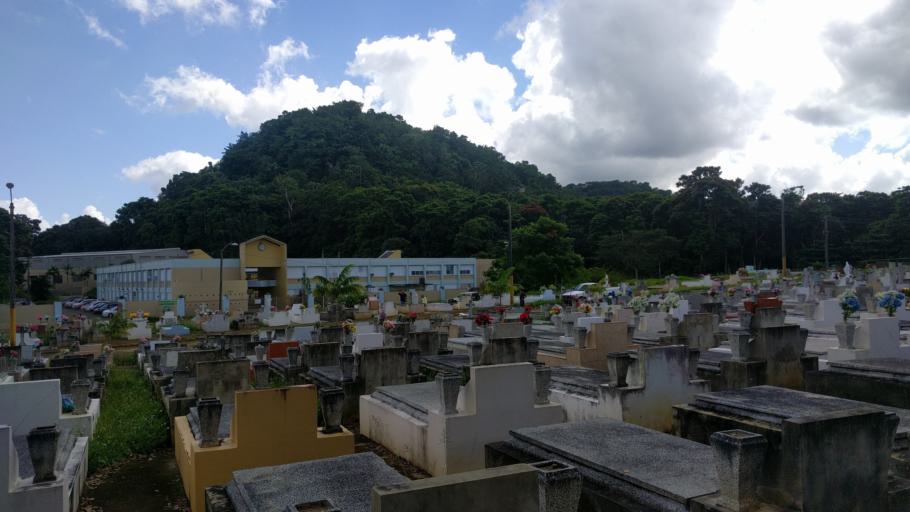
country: PR
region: Florida
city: Estancias de Florida
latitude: 18.3643
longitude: -66.5729
